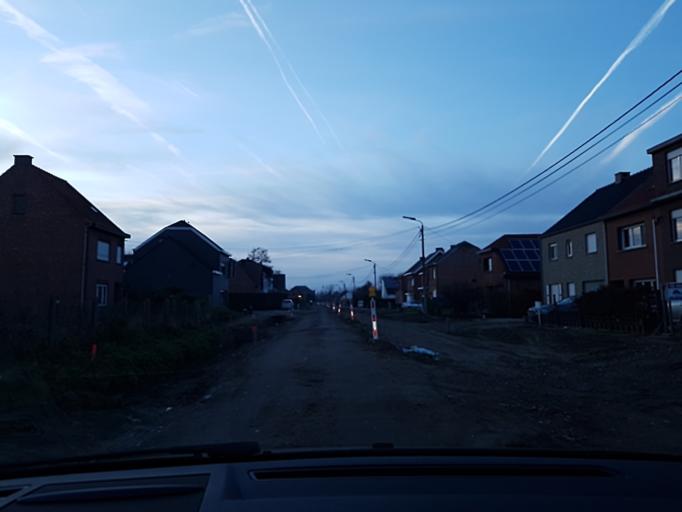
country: BE
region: Flanders
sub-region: Provincie Vlaams-Brabant
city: Haacht
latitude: 50.9736
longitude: 4.6496
